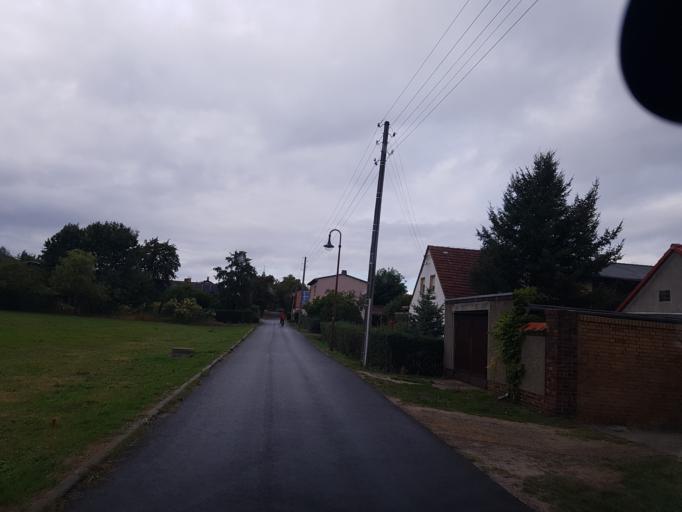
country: DE
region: Brandenburg
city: Finsterwalde
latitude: 51.6246
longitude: 13.7700
